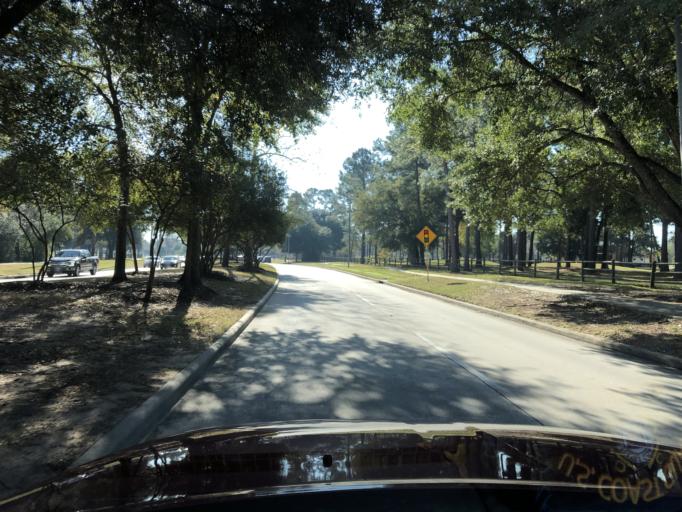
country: US
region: Texas
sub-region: Harris County
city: Tomball
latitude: 30.0386
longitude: -95.5625
